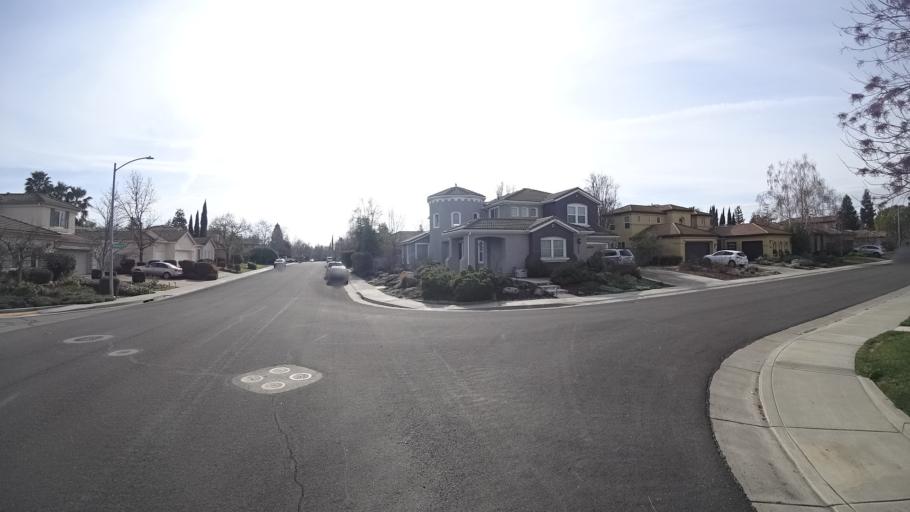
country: US
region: California
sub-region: Yolo County
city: Davis
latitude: 38.5514
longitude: -121.6818
